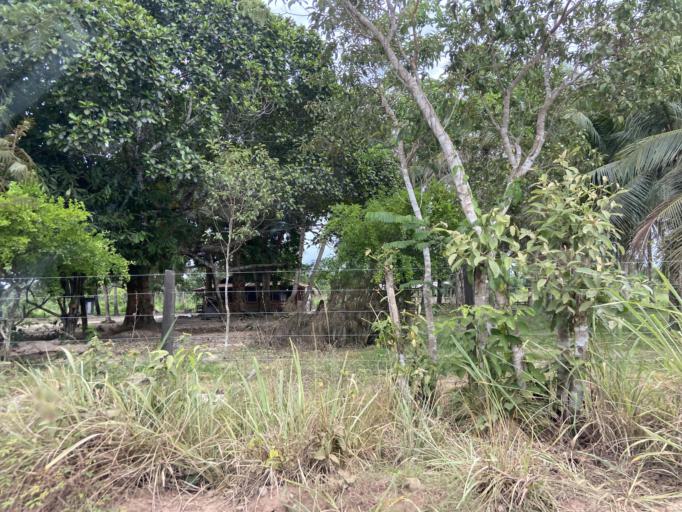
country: BR
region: Para
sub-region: Maraba
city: Maraba
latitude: -5.2647
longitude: -49.0036
